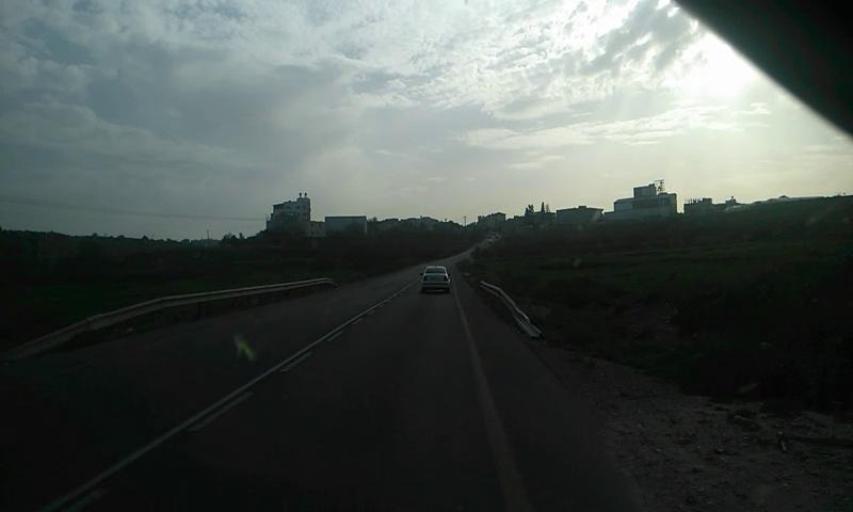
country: PS
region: West Bank
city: Hajjah
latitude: 32.1931
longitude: 35.1402
